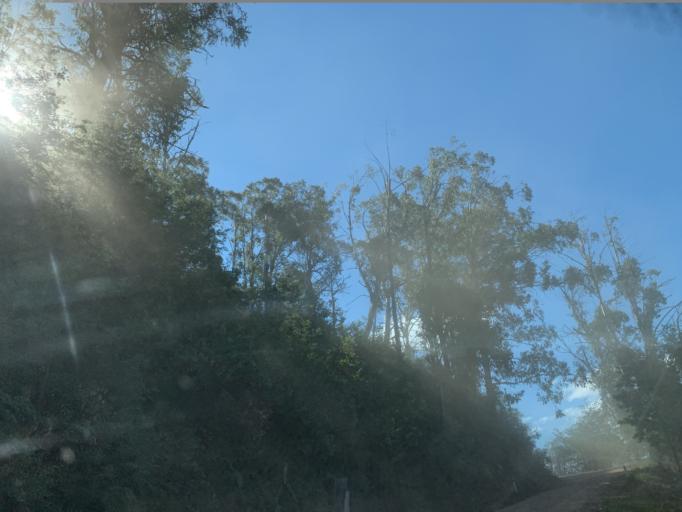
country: AU
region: Victoria
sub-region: Mansfield
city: Mansfield
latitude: -37.0981
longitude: 146.4984
